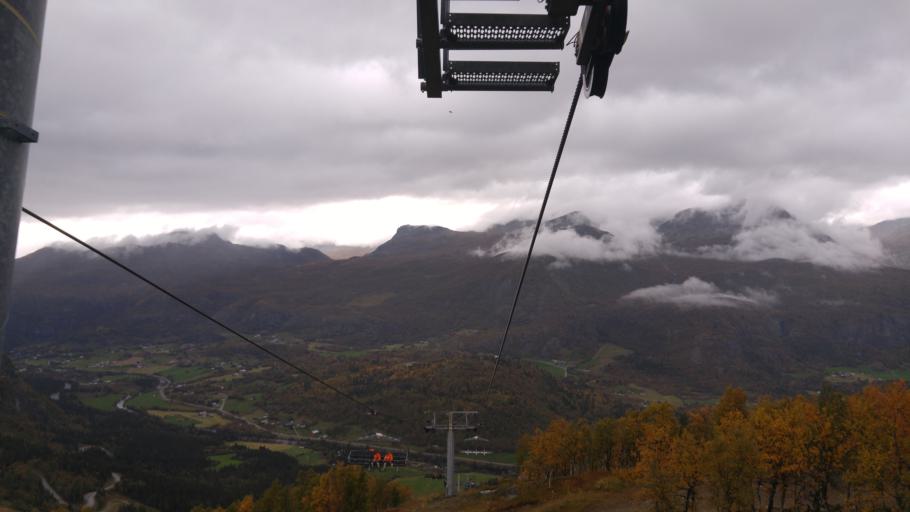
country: NO
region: Buskerud
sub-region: Hemsedal
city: Hemsedal
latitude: 60.8519
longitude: 8.5120
